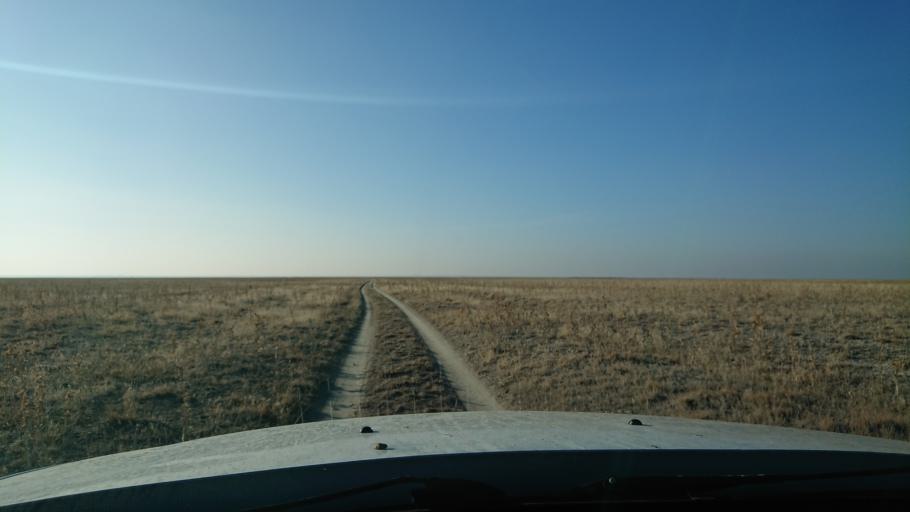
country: TR
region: Aksaray
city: Sultanhani
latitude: 38.3713
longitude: 33.5549
